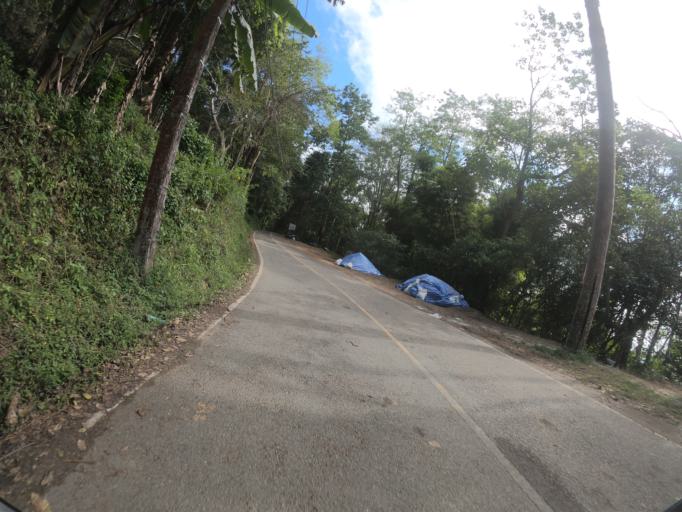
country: TH
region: Chiang Mai
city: Chiang Mai
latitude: 18.8145
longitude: 98.8819
